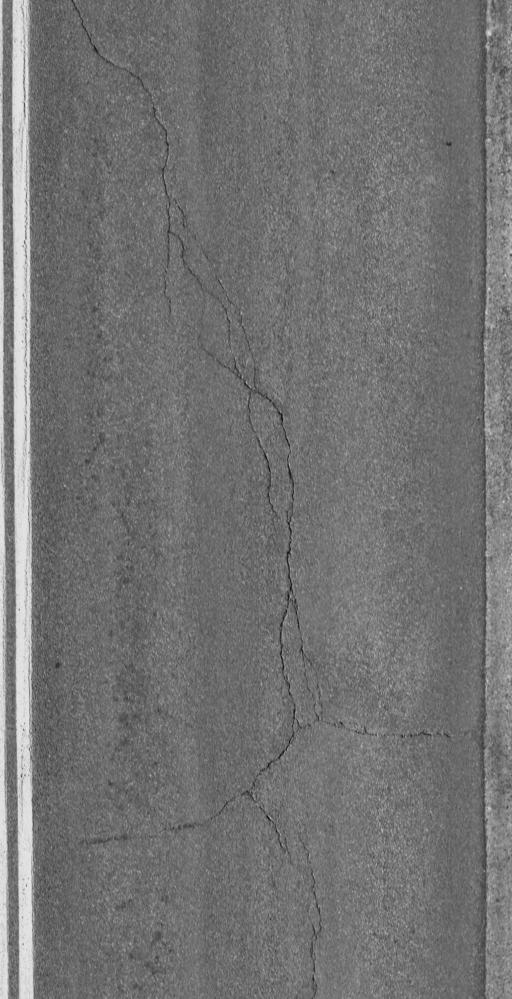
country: US
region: Vermont
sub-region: Chittenden County
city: Hinesburg
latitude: 44.3822
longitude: -73.1772
